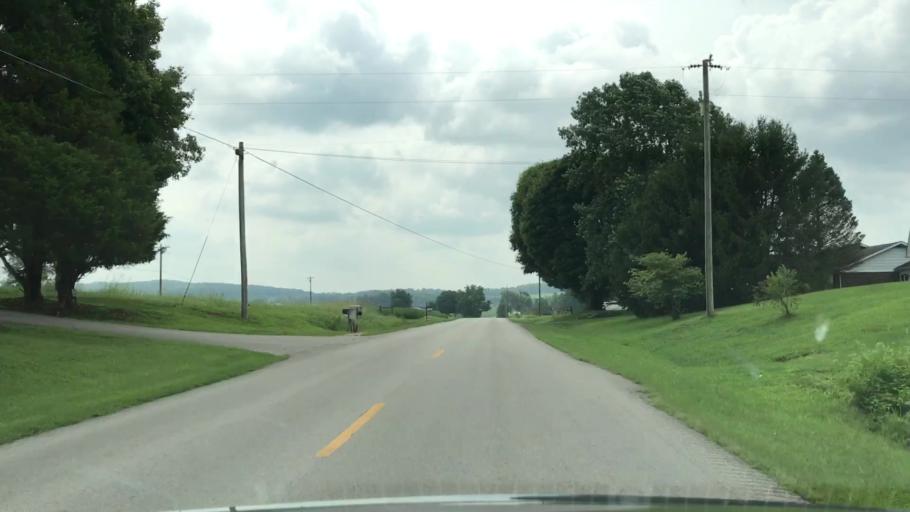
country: US
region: Kentucky
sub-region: Barren County
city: Cave City
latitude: 37.1039
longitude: -85.9789
